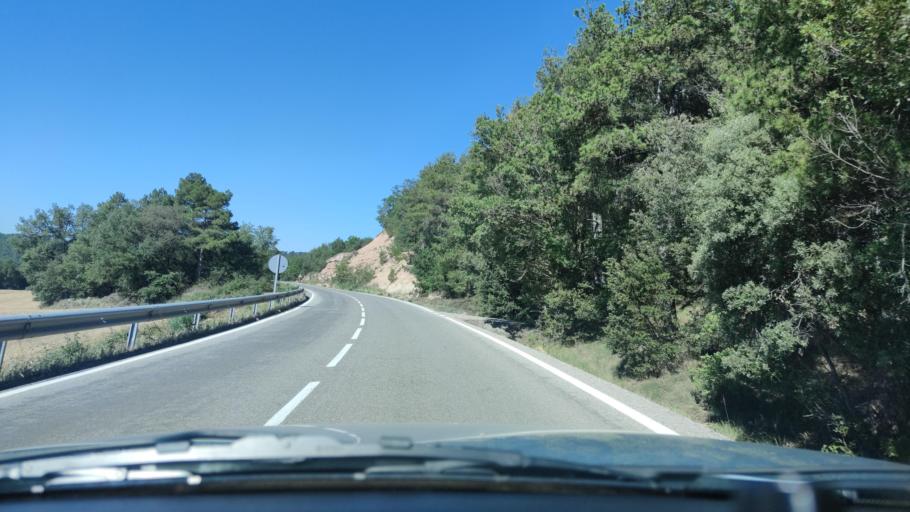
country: ES
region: Catalonia
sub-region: Provincia de Barcelona
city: Cardona
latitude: 41.8914
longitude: 1.5722
